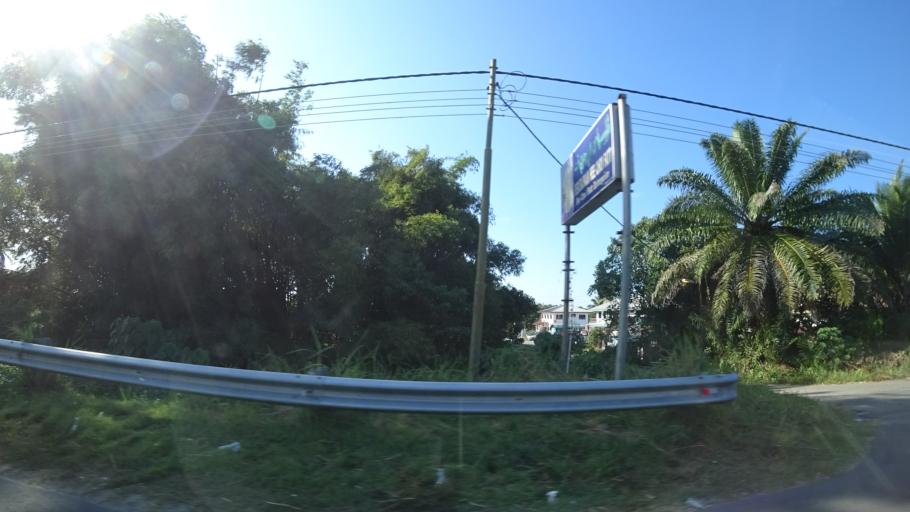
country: BN
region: Tutong
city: Tutong
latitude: 4.6919
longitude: 114.5135
